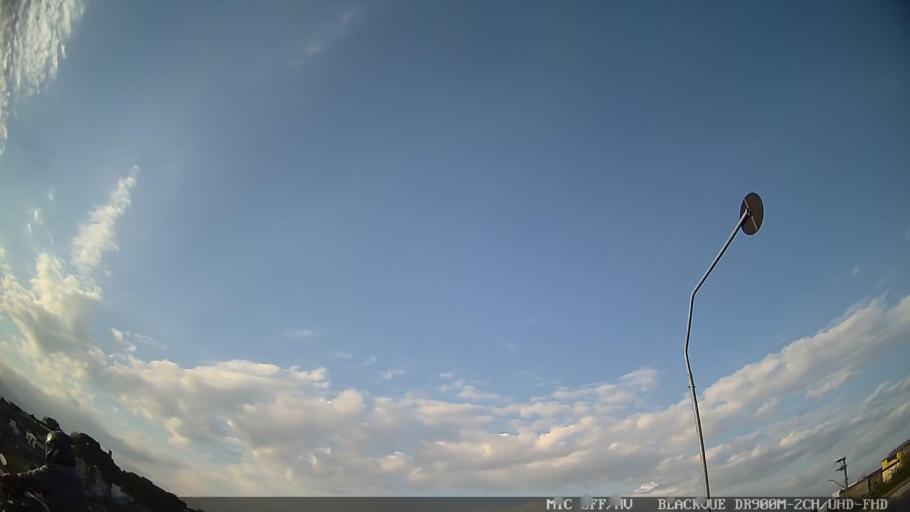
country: BR
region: Sao Paulo
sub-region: Ferraz De Vasconcelos
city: Ferraz de Vasconcelos
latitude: -23.5249
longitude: -46.4341
